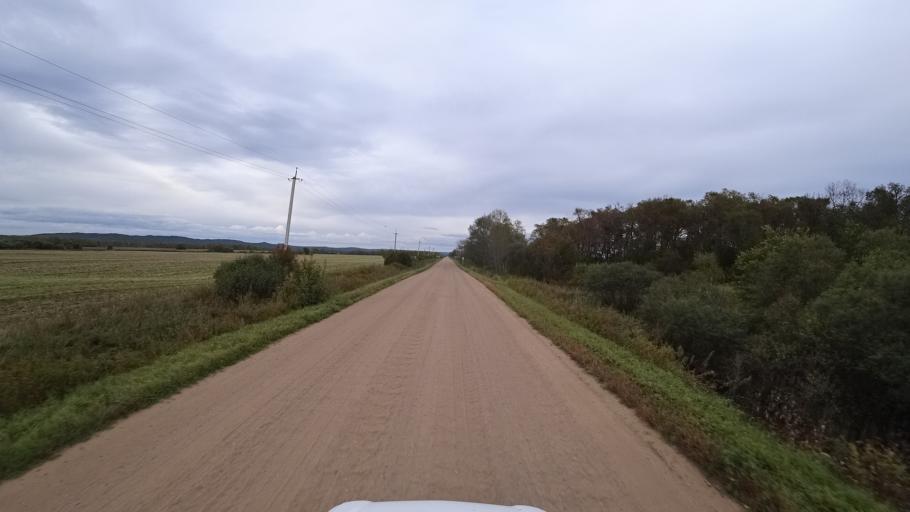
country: RU
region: Amur
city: Arkhara
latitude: 49.4346
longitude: 130.2550
